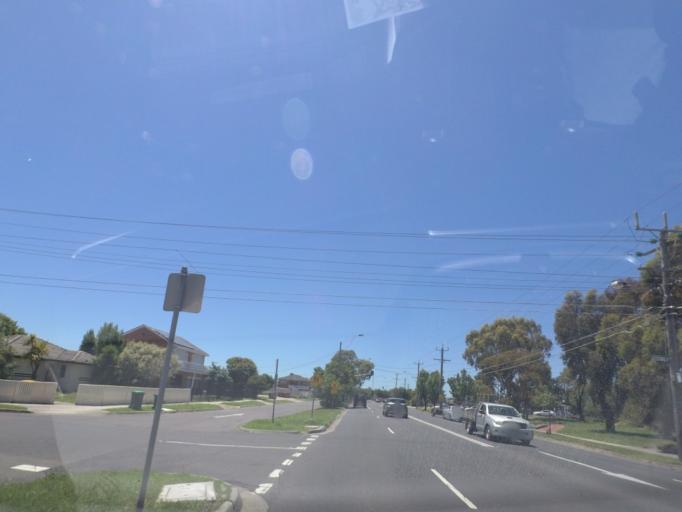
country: AU
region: Victoria
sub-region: Whittlesea
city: Lalor
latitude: -37.6671
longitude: 145.0162
